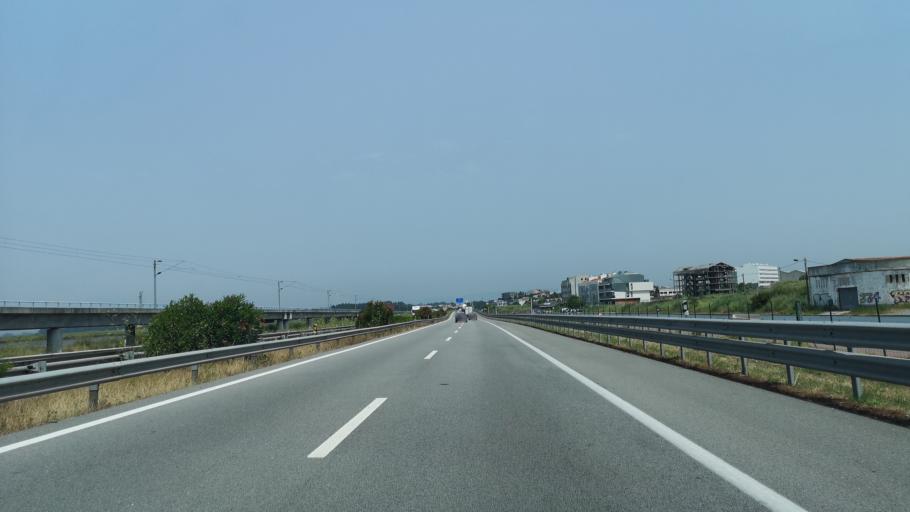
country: PT
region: Aveiro
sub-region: Aveiro
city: Aveiro
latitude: 40.6487
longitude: -8.6493
